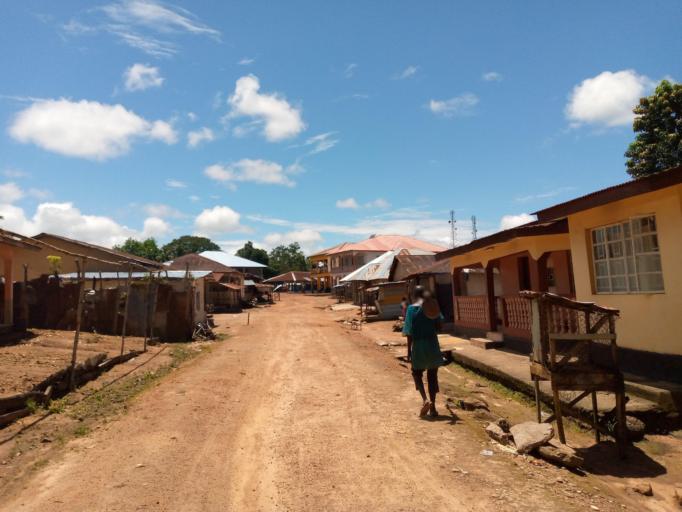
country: SL
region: Northern Province
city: Makeni
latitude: 9.0340
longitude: -12.1596
